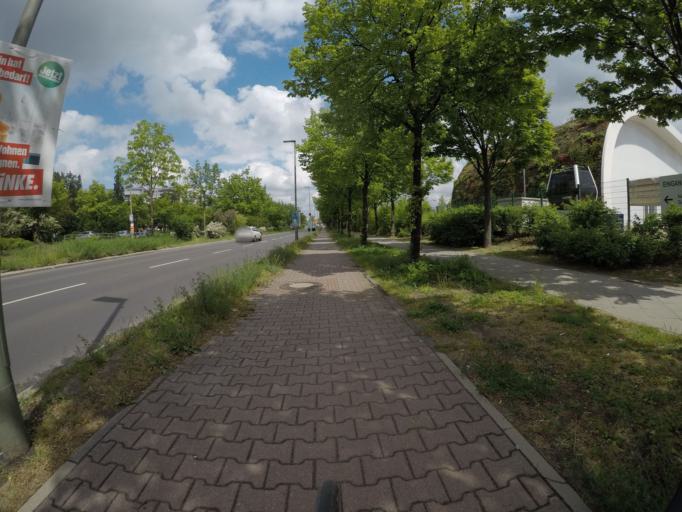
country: DE
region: Berlin
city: Marzahn
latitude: 52.5359
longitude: 13.5674
